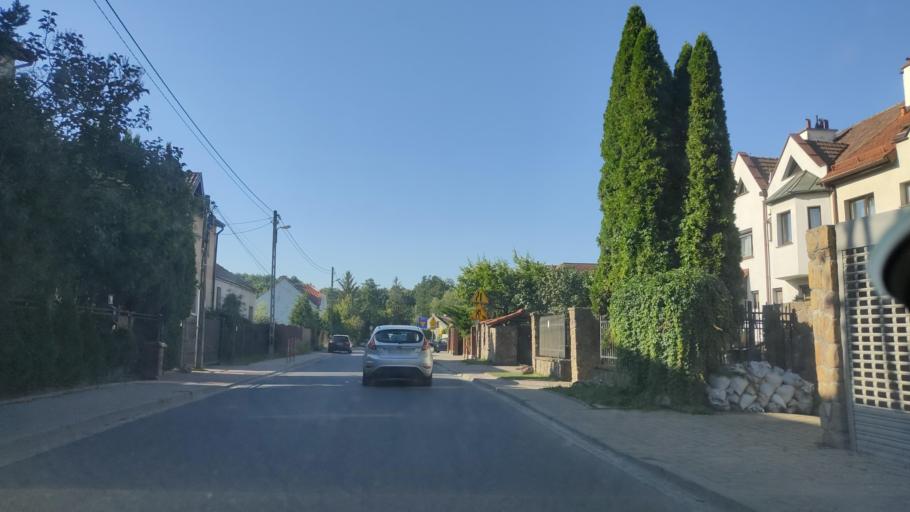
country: PL
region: Lesser Poland Voivodeship
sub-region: Powiat krakowski
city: Zielonki
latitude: 50.0971
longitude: 19.9409
